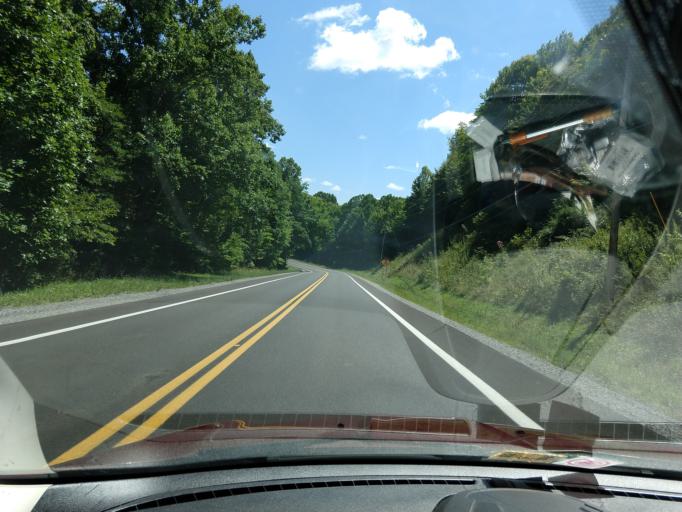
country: US
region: West Virginia
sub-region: Fayette County
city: Fayetteville
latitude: 38.0679
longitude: -80.9763
